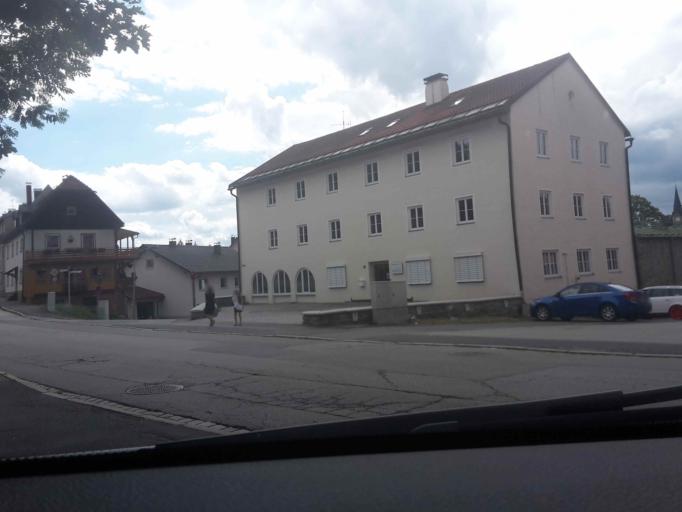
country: DE
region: Bavaria
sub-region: Lower Bavaria
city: Zwiesel
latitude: 49.0195
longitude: 13.2316
